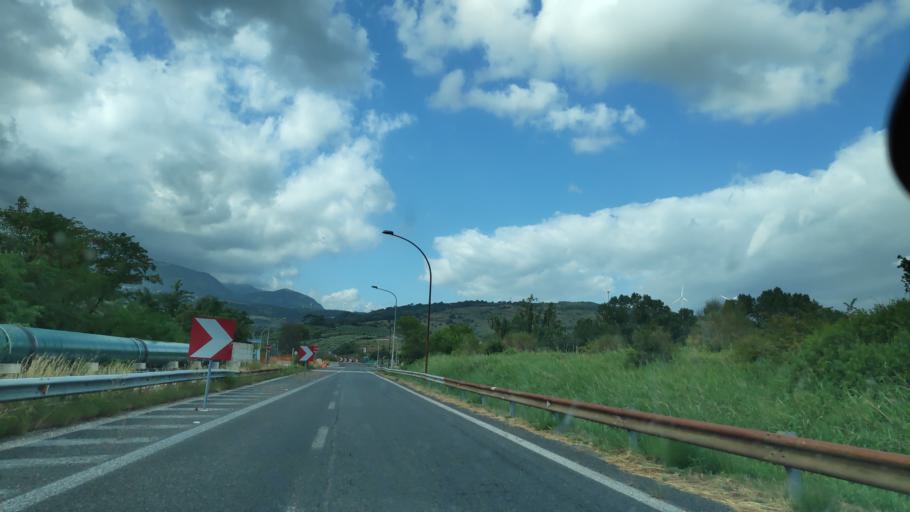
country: IT
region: Campania
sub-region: Provincia di Salerno
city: Serre
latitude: 40.6208
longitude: 15.1816
